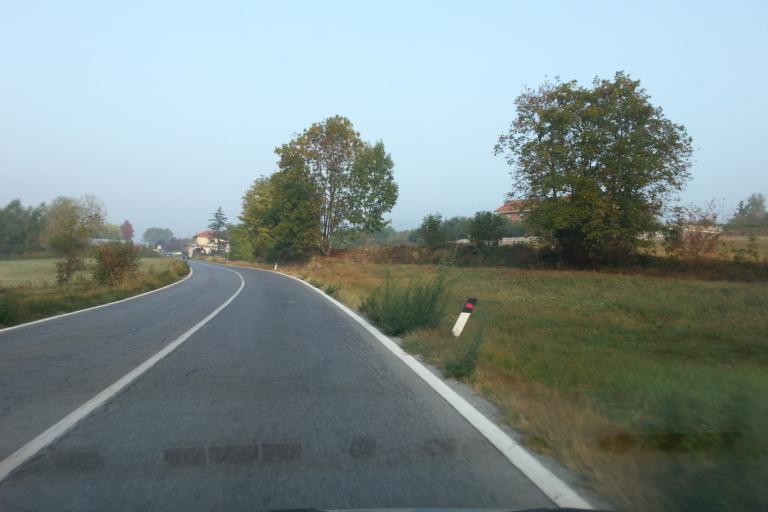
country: IT
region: Piedmont
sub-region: Provincia di Torino
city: Giaveno
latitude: 45.0404
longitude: 7.3809
